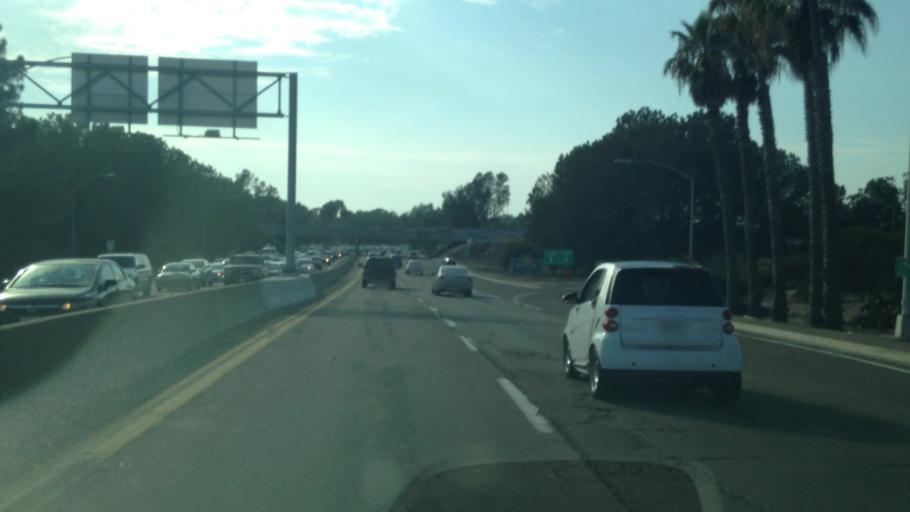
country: US
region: California
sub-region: San Diego County
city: San Diego
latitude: 32.7599
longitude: -117.2277
